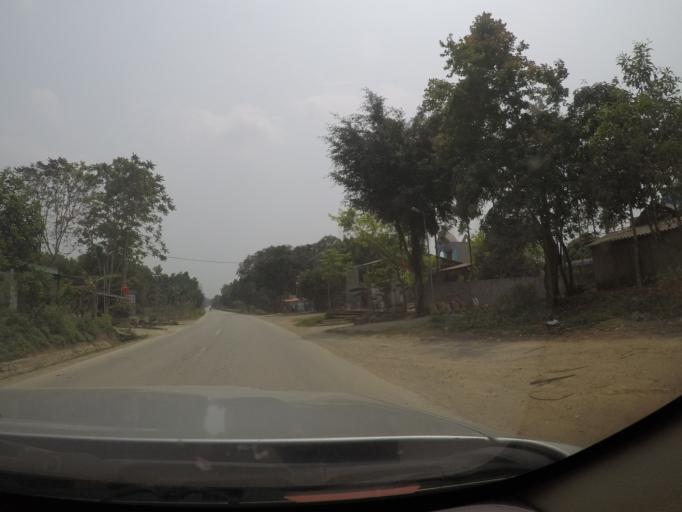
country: VN
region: Thanh Hoa
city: Thi Tran Yen Cat
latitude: 19.7731
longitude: 105.4081
